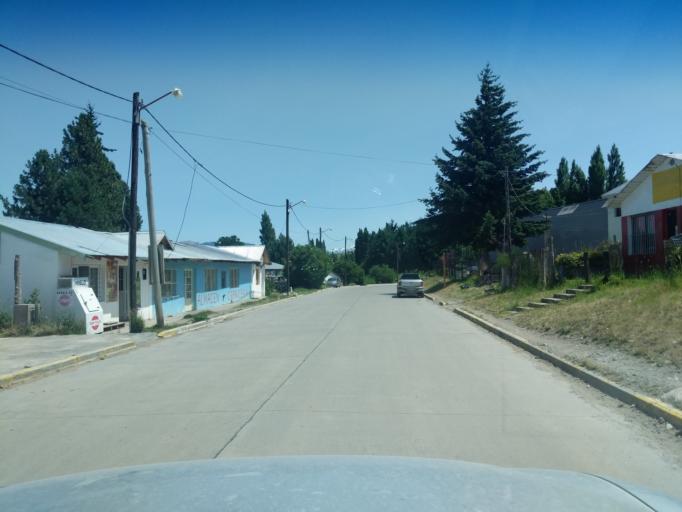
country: CL
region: Los Lagos
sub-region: Provincia de Palena
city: Palena
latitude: -43.5364
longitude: -71.4699
